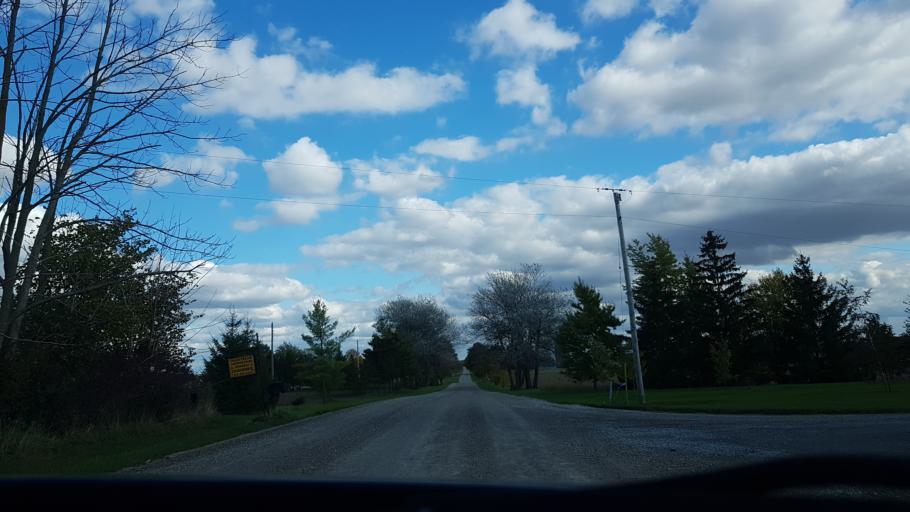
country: CA
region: Ontario
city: South Huron
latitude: 43.1107
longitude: -81.6359
